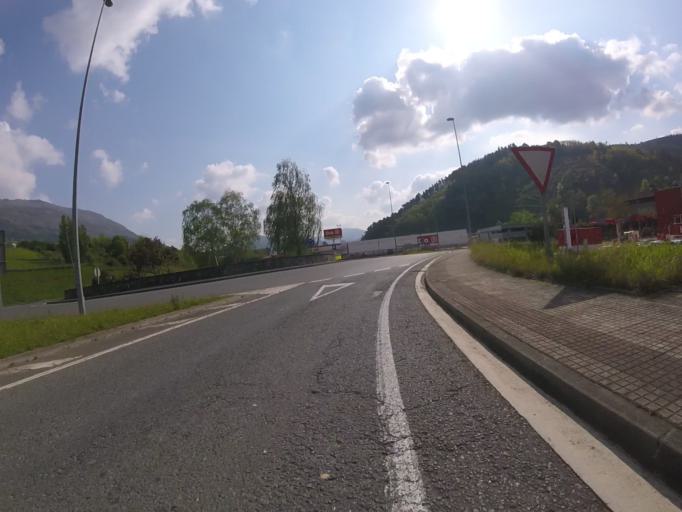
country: ES
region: Basque Country
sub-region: Provincia de Guipuzcoa
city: Azkoitia
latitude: 43.1727
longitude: -2.3040
